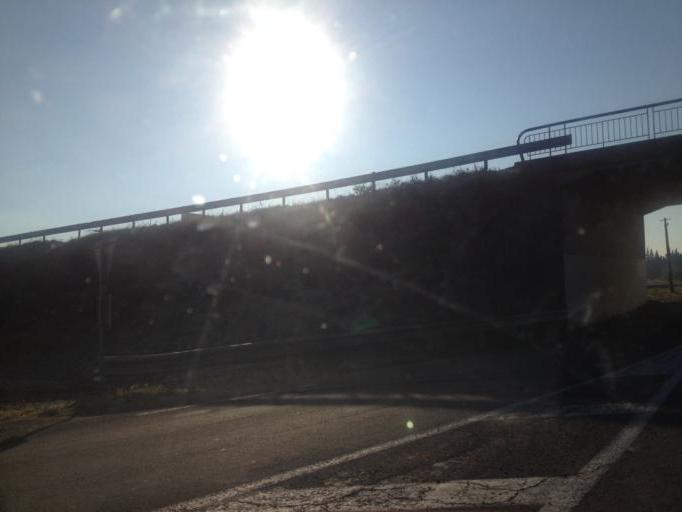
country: FR
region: Rhone-Alpes
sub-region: Departement de la Drome
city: Pierrelatte
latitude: 44.3608
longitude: 4.6931
